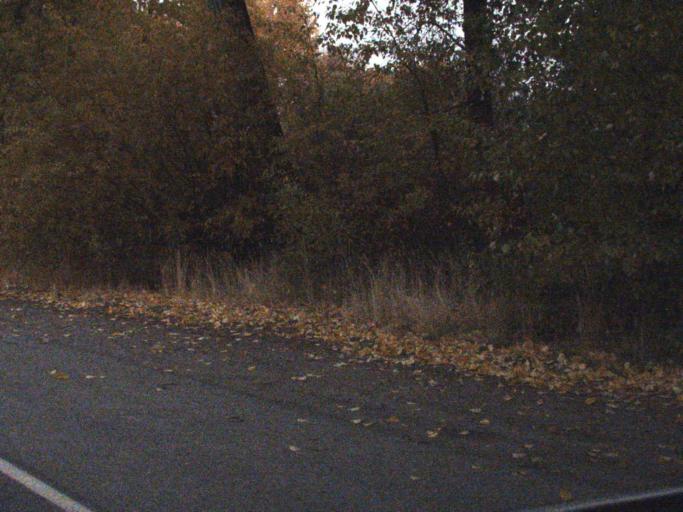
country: US
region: Washington
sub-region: Stevens County
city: Colville
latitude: 48.5734
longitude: -117.9460
